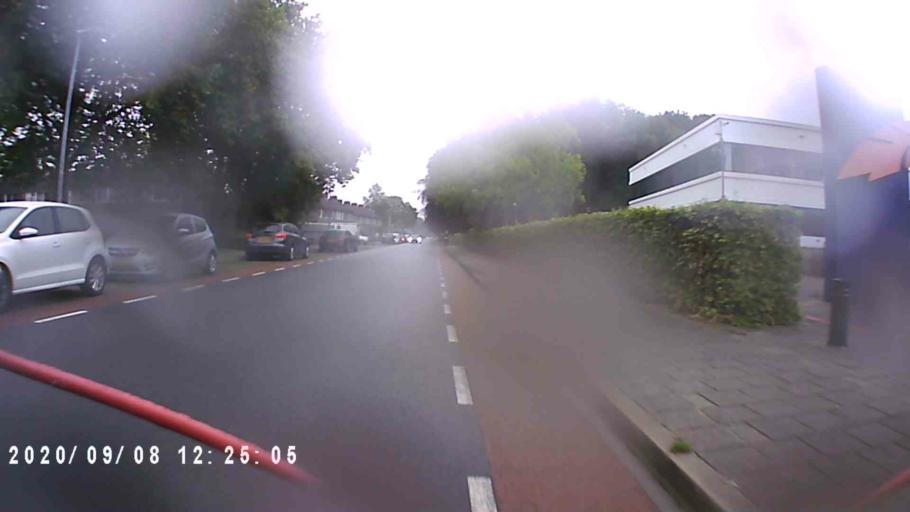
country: NL
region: Groningen
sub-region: Gemeente Veendam
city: Veendam
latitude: 53.0965
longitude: 6.8646
